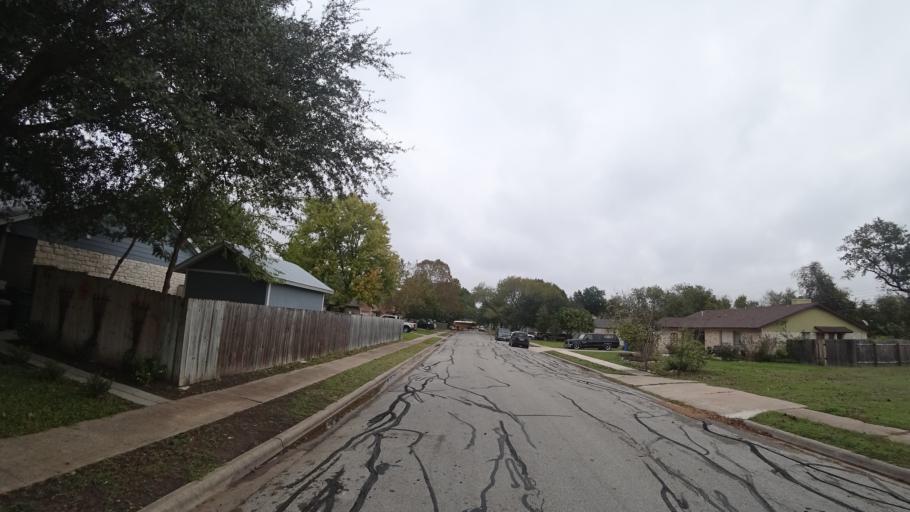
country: US
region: Texas
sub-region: Travis County
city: Pflugerville
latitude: 30.4261
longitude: -97.6082
